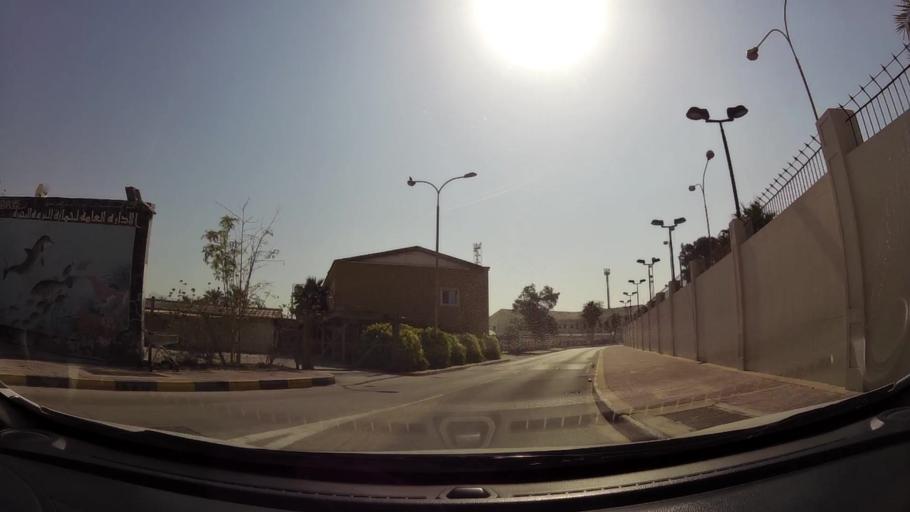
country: BH
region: Manama
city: Manama
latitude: 26.2095
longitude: 50.6046
